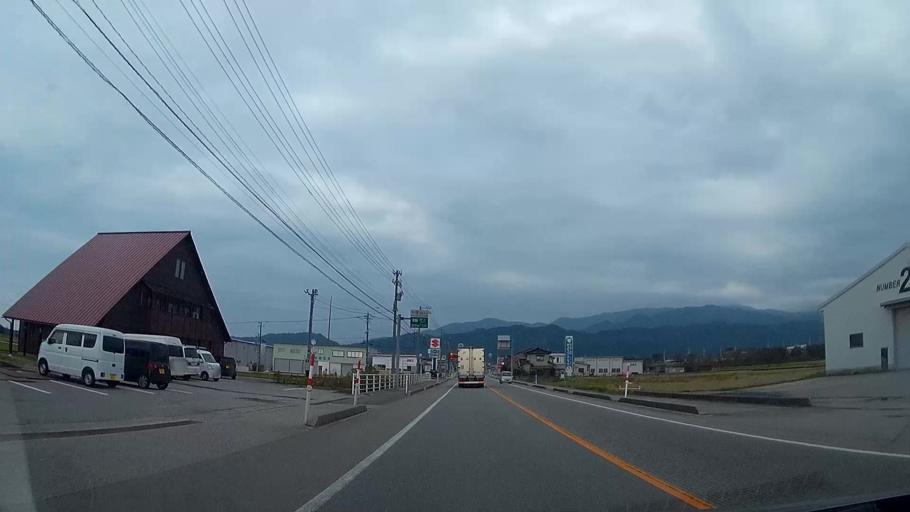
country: JP
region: Toyama
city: Nyuzen
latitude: 36.9462
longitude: 137.5434
